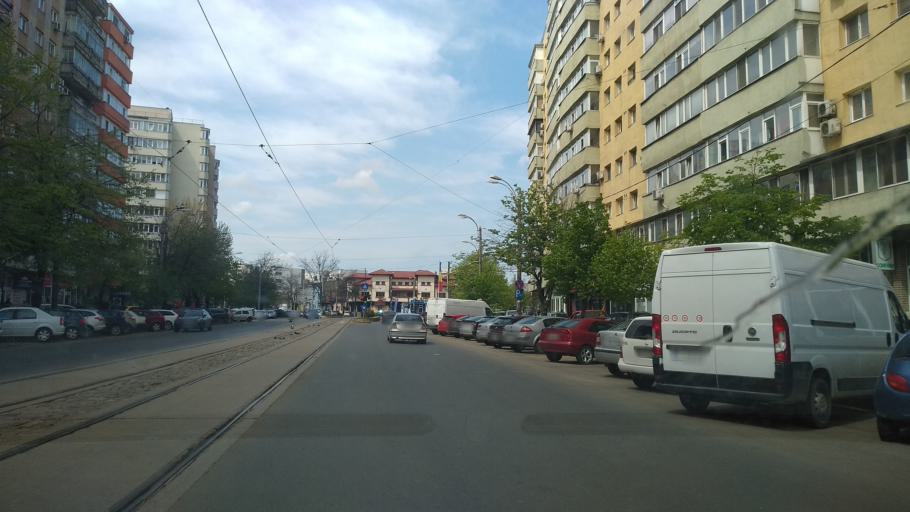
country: RO
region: Ilfov
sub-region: Comuna Fundeni-Dobroesti
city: Fundeni
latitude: 44.4446
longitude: 26.1381
